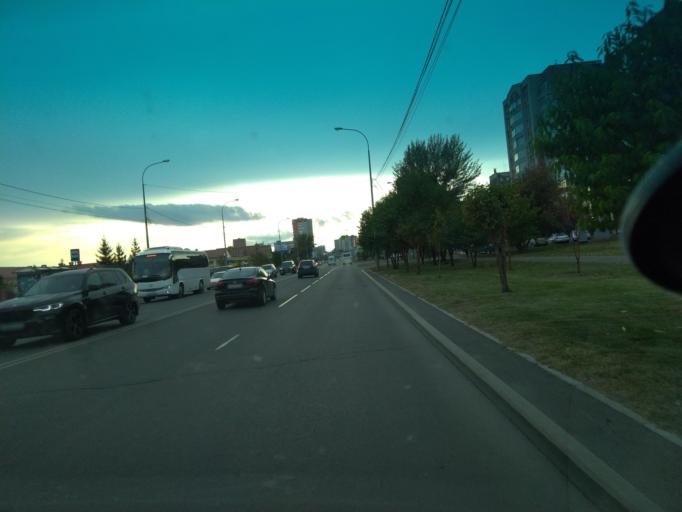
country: RU
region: Krasnoyarskiy
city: Krasnoyarsk
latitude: 56.0338
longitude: 92.9046
